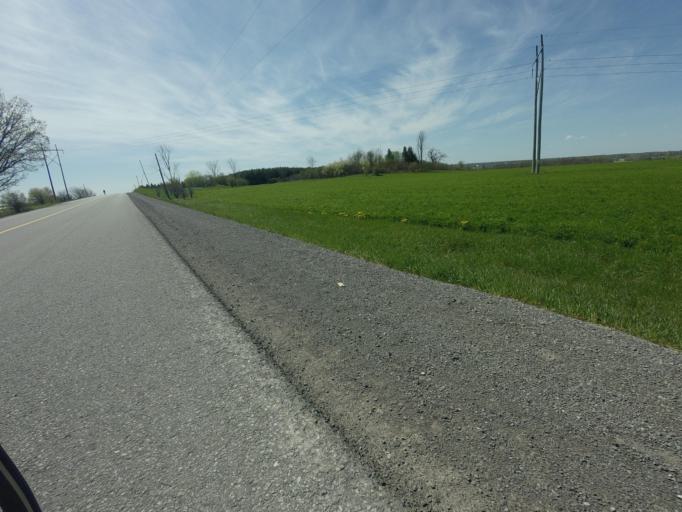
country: CA
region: Ontario
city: Arnprior
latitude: 45.4056
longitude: -76.1596
